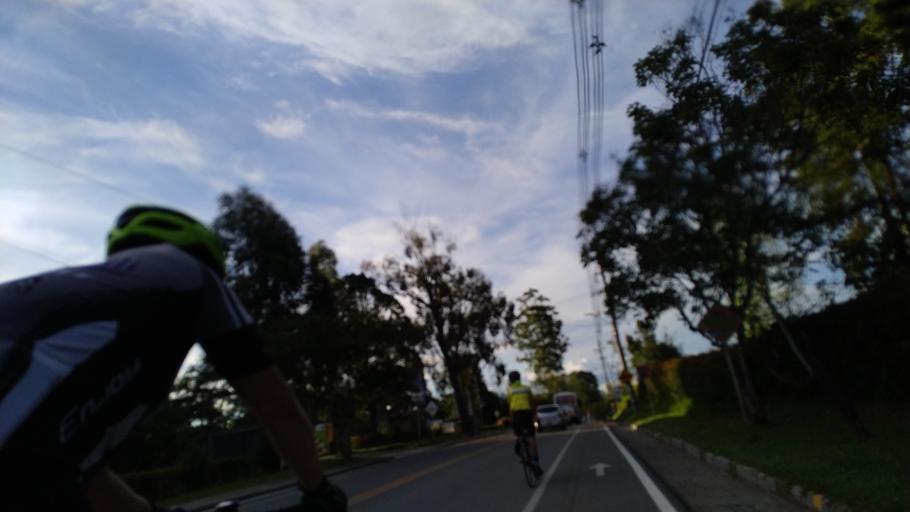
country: CO
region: Antioquia
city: Rionegro
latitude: 6.1349
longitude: -75.3783
